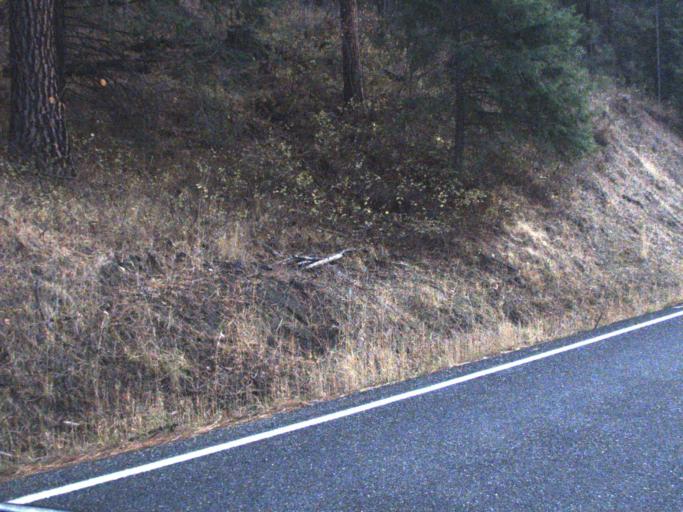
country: US
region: Washington
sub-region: Stevens County
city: Kettle Falls
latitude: 48.2325
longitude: -118.1540
